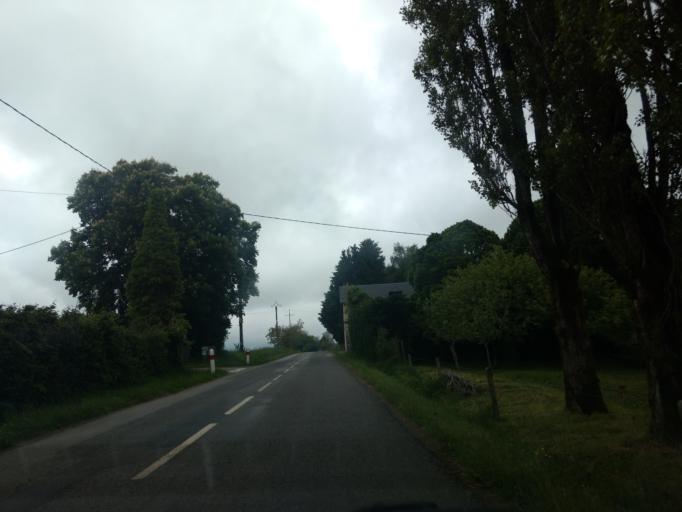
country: FR
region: Midi-Pyrenees
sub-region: Departement de l'Aveyron
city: Viviez
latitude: 44.5157
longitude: 2.1841
